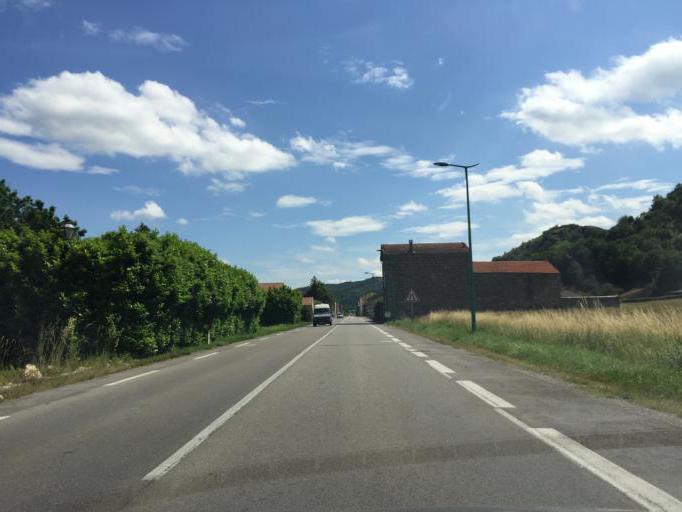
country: FR
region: Rhone-Alpes
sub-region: Departement de l'Ardeche
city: Sarras
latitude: 45.2014
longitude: 4.8016
